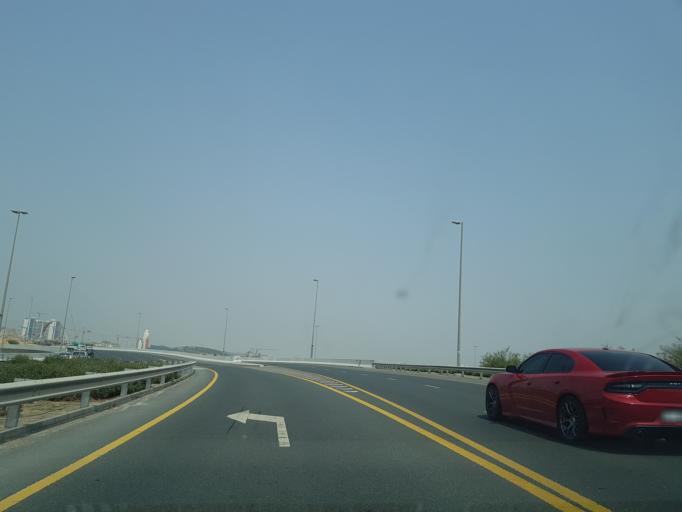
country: AE
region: Dubai
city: Dubai
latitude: 25.0579
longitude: 55.2512
